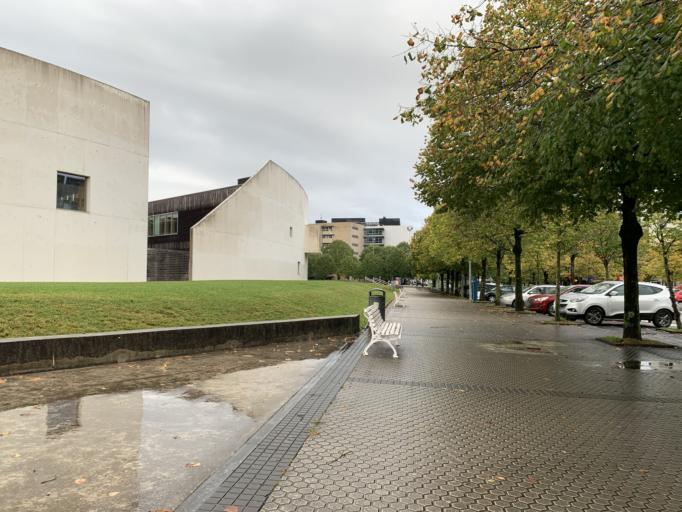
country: ES
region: Basque Country
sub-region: Provincia de Guipuzcoa
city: San Sebastian
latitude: 43.3080
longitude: -2.0118
